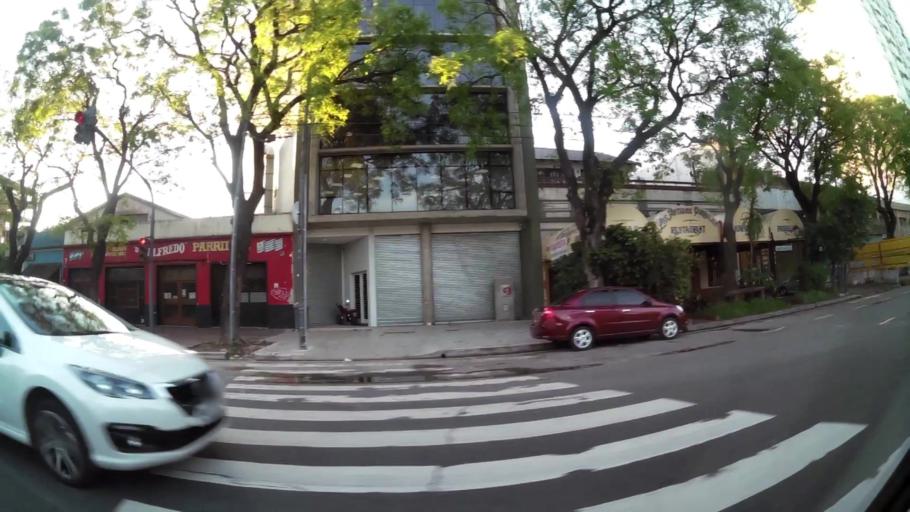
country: AR
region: Buenos Aires F.D.
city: Buenos Aires
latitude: -34.6393
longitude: -58.4117
